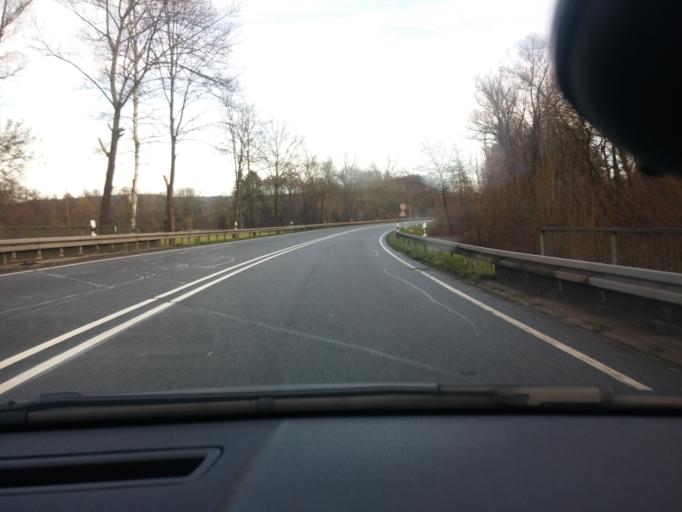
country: DE
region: Hesse
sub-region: Regierungsbezirk Darmstadt
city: Bad Konig
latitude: 49.7427
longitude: 8.9944
